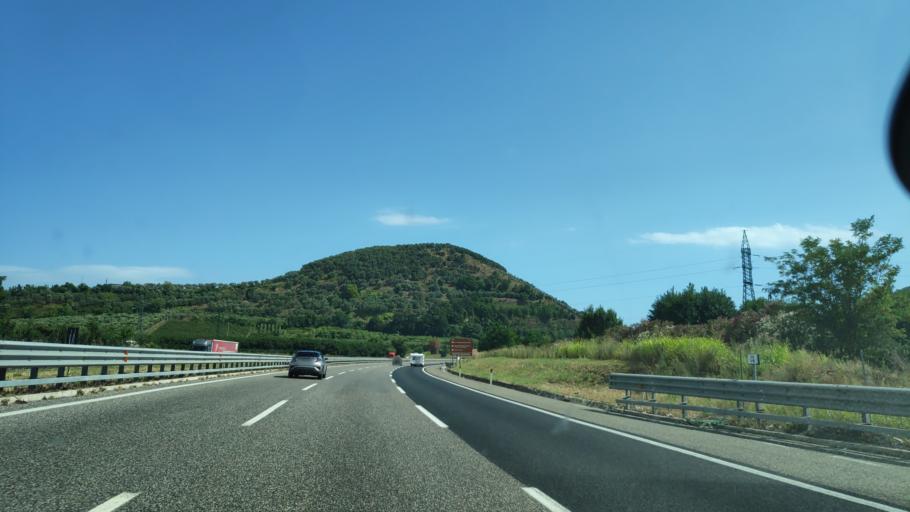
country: IT
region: Campania
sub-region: Provincia di Salerno
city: Pezzano-Filetta
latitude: 40.6824
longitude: 14.8559
